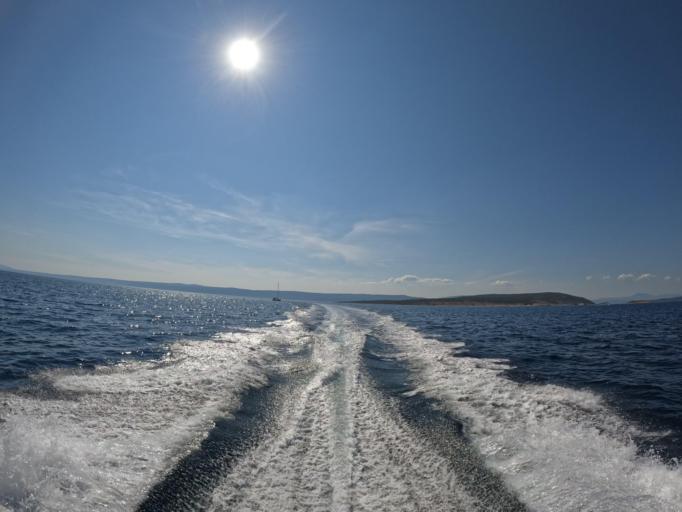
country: HR
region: Primorsko-Goranska
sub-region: Grad Krk
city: Krk
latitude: 44.9542
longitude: 14.5693
